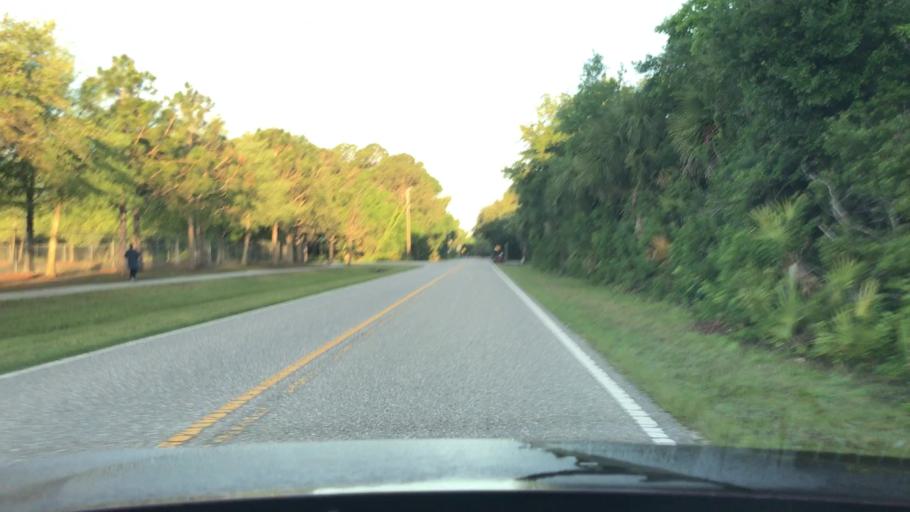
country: US
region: Florida
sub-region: Sarasota County
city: Fruitville
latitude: 27.3274
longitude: -82.4196
